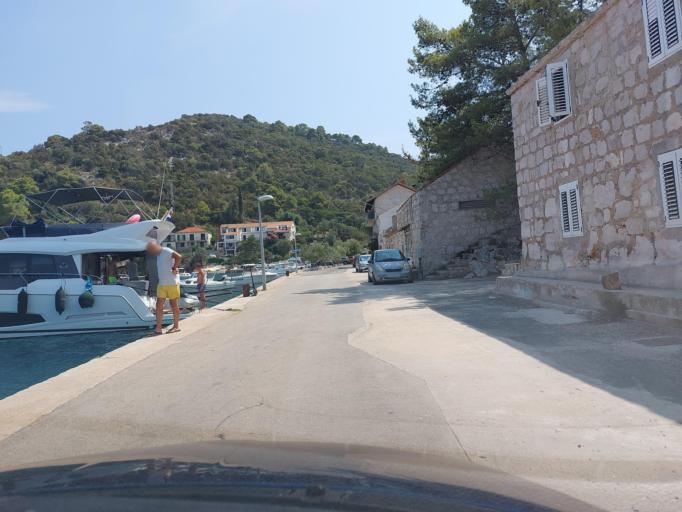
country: HR
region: Dubrovacko-Neretvanska
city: Smokvica
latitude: 42.7729
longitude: 16.8738
